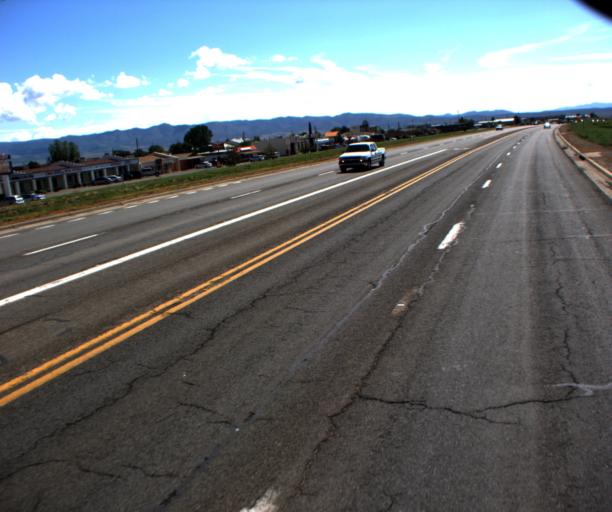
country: US
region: Arizona
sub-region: Yavapai County
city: Prescott Valley
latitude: 34.5854
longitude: -112.3172
